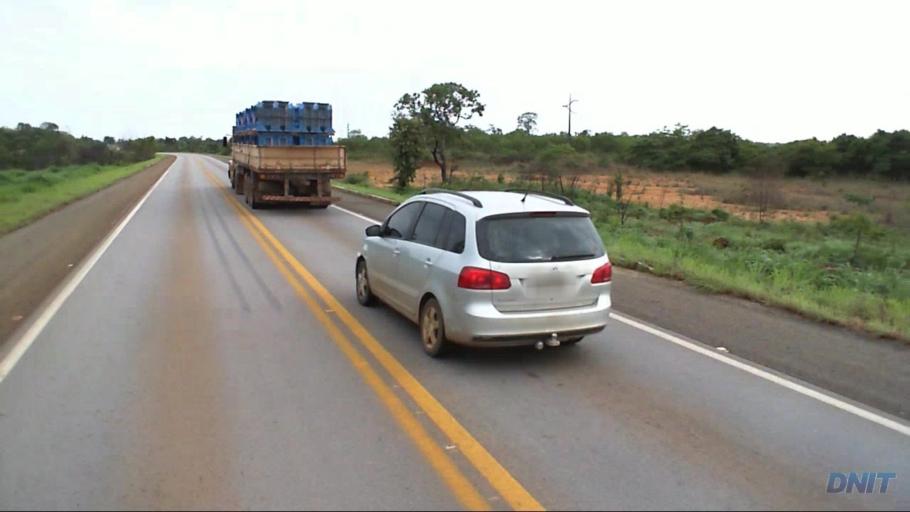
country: BR
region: Goias
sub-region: Uruacu
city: Uruacu
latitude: -14.7394
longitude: -49.0836
